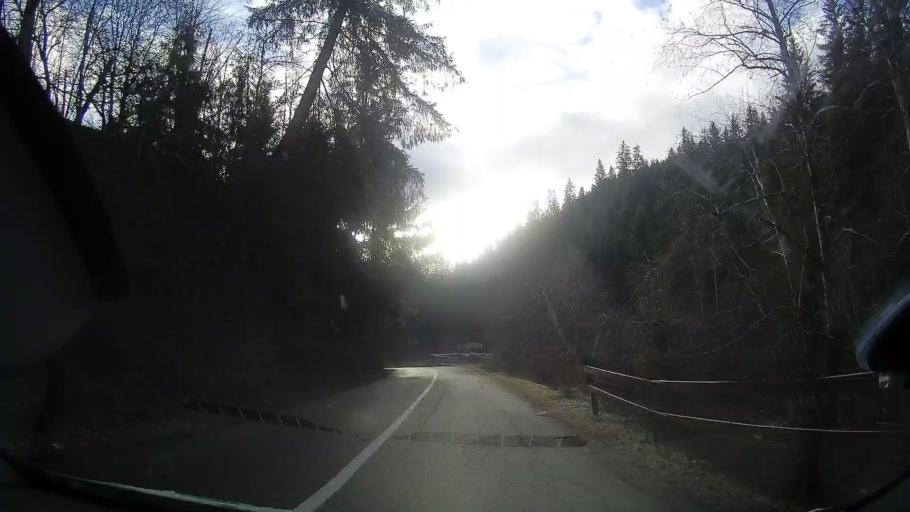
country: RO
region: Alba
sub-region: Comuna Albac
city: Albac
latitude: 46.4762
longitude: 22.9612
